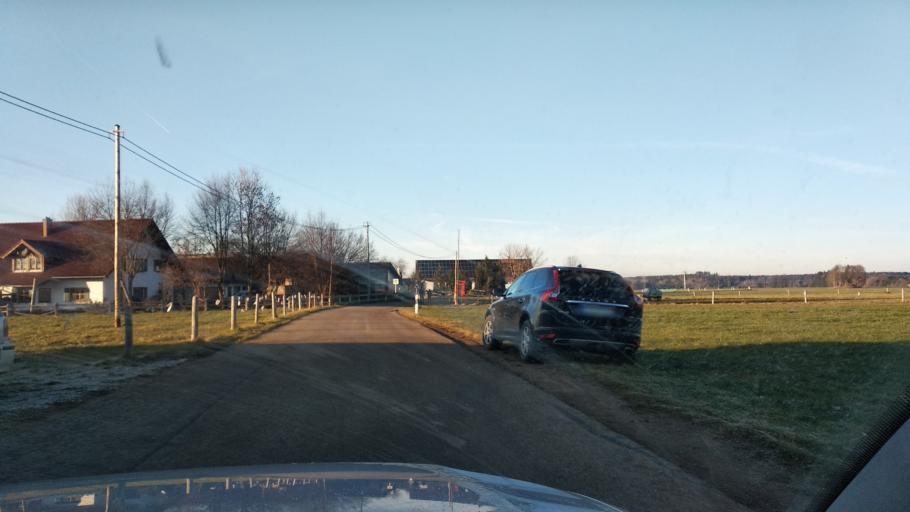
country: DE
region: Bavaria
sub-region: Swabia
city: Lautrach
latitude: 47.9143
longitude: 10.1309
